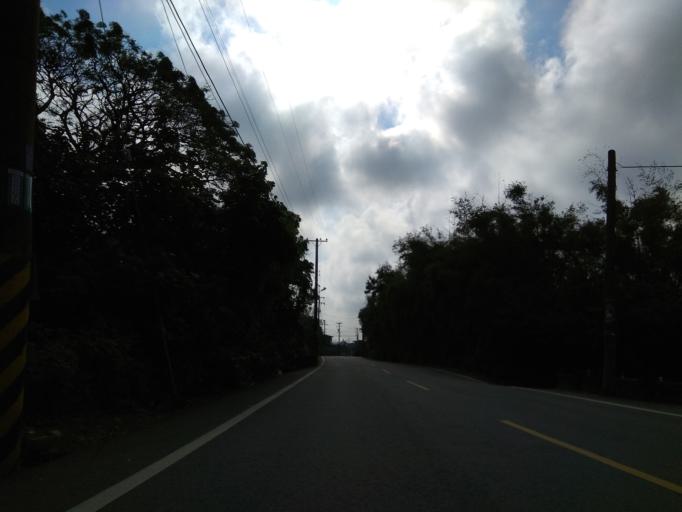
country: TW
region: Taiwan
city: Taoyuan City
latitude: 25.0573
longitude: 121.1509
